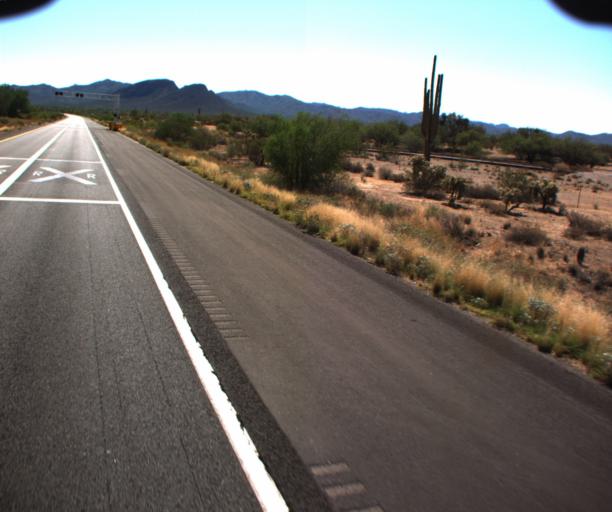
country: US
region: Arizona
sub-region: Pinal County
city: Gold Camp
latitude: 33.2576
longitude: -111.3035
